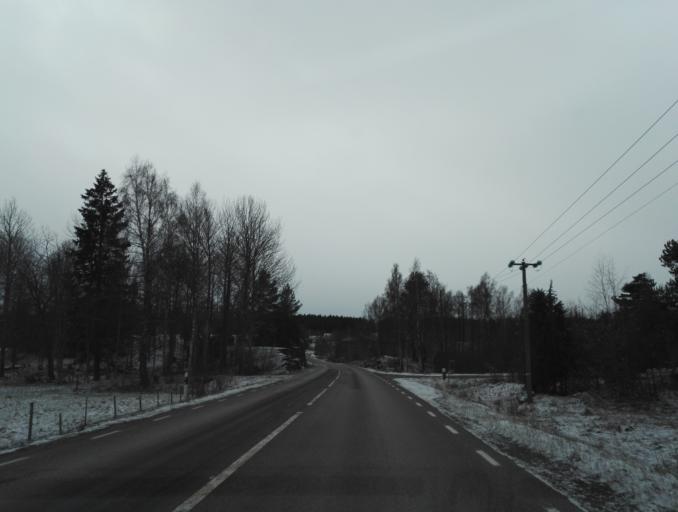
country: SE
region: Kalmar
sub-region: Hultsfreds Kommun
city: Virserum
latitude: 57.2906
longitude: 15.5654
